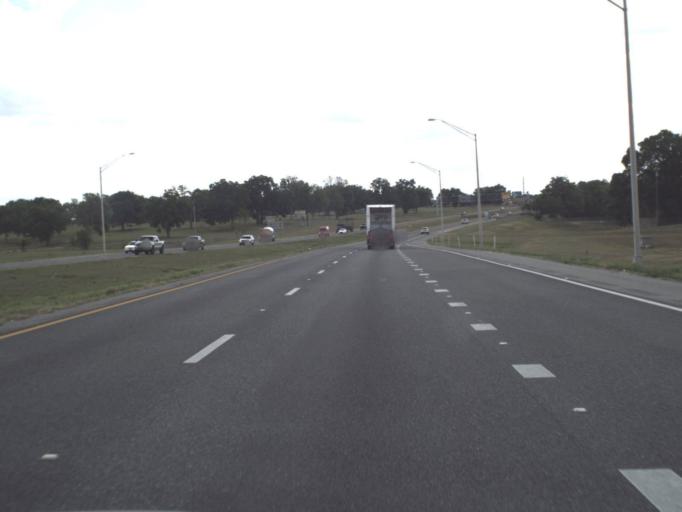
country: US
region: Florida
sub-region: Orange County
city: Paradise Heights
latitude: 28.6291
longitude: -81.5388
